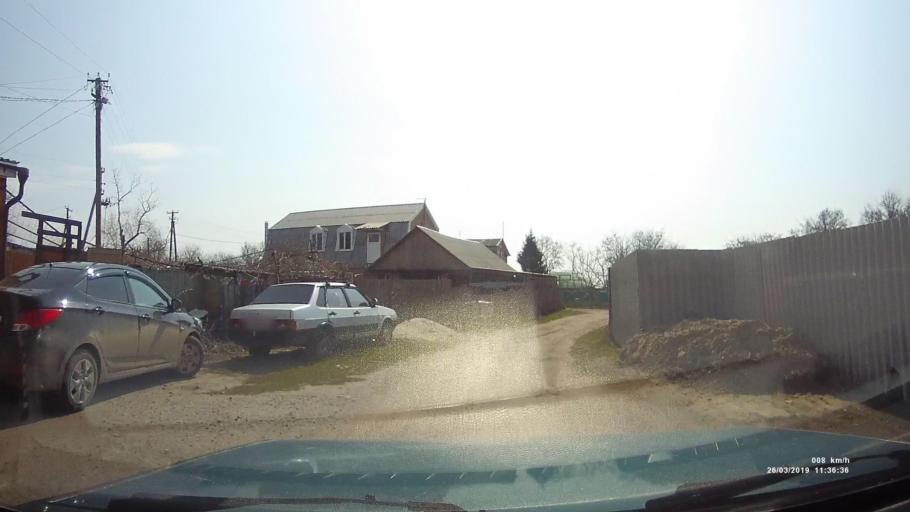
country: RU
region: Rostov
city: Novobessergenovka
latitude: 47.1465
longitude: 38.6426
